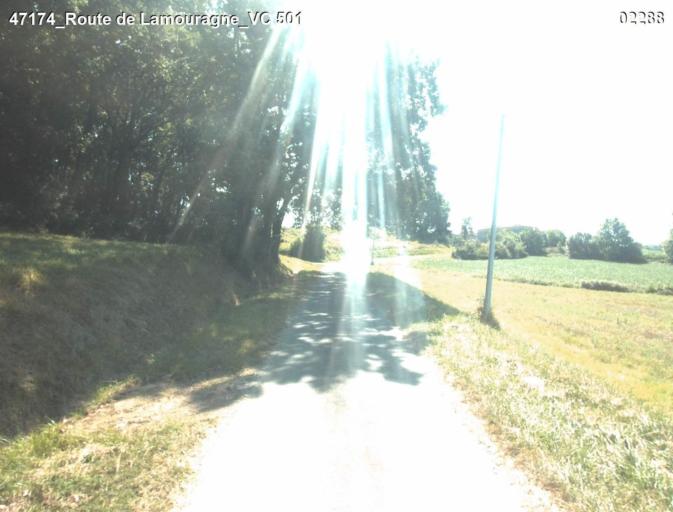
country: FR
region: Midi-Pyrenees
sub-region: Departement du Gers
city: Condom
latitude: 44.0289
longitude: 0.3952
